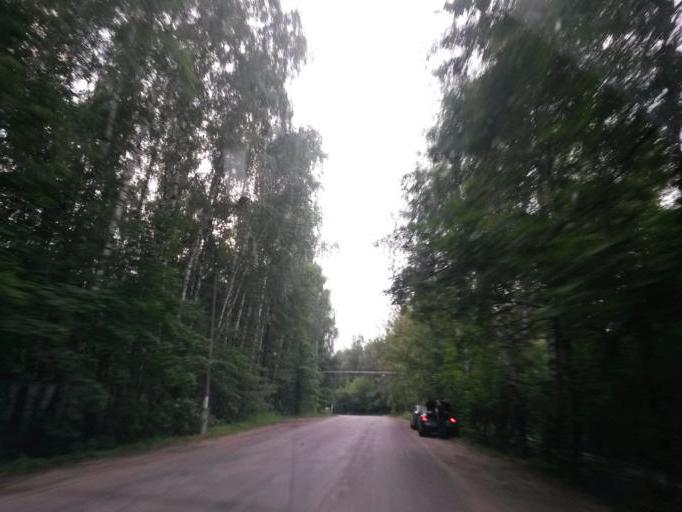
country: RU
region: Moskovskaya
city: Lyubuchany
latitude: 55.2487
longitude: 37.6355
